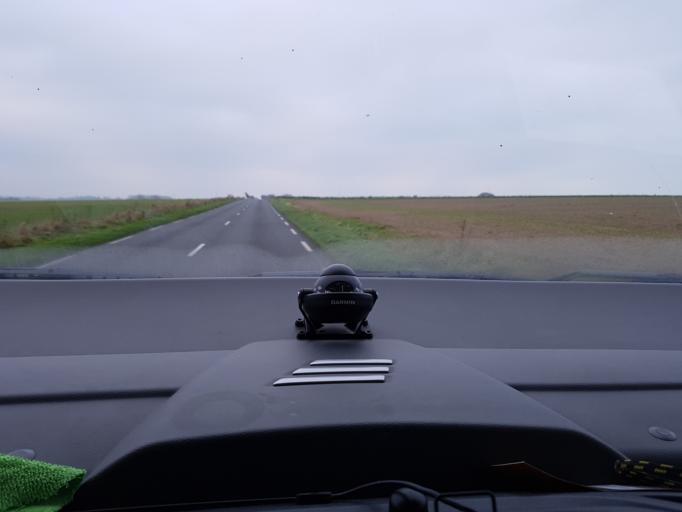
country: FR
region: Picardie
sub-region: Departement de la Somme
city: Ault
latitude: 50.1035
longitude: 1.4727
